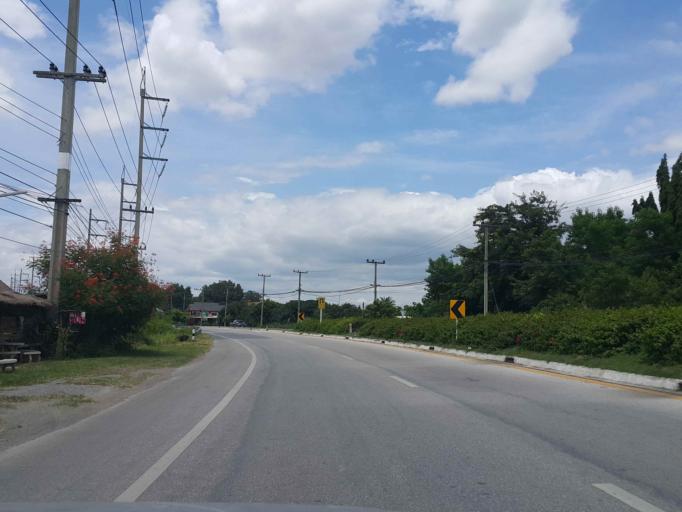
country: TH
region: Lamphun
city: Ban Hong
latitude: 18.3147
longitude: 98.8238
